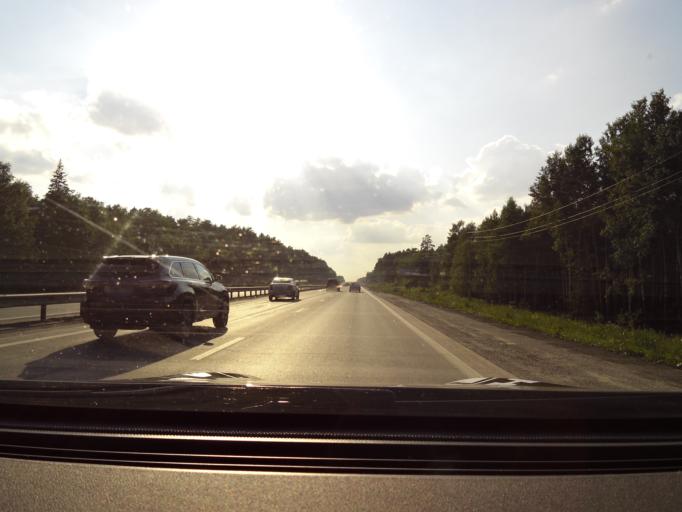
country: RU
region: Sverdlovsk
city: Severka
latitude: 56.8371
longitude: 60.2799
